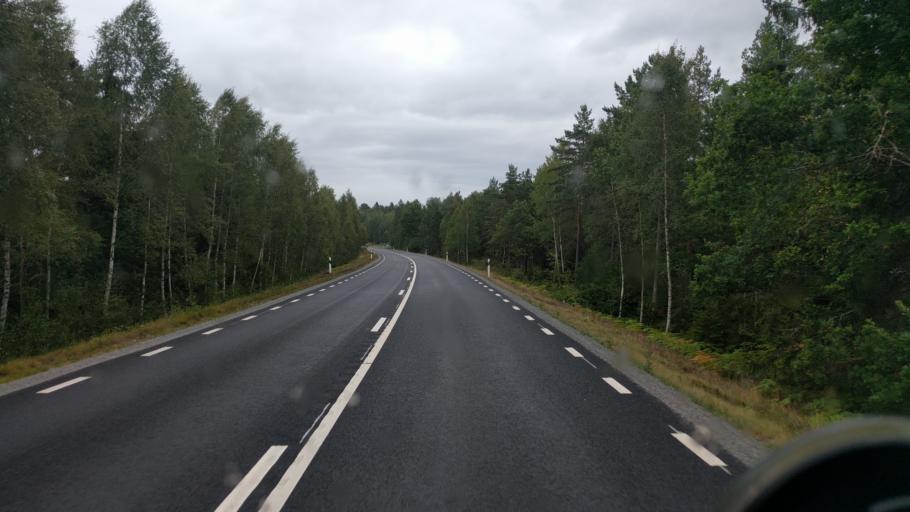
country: SE
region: Kalmar
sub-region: Vasterviks Kommun
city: Ankarsrum
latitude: 57.7219
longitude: 16.4306
